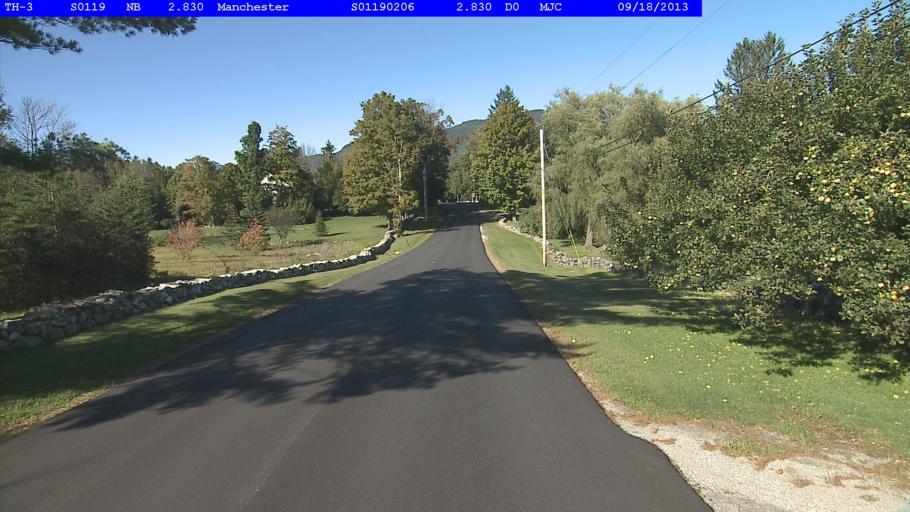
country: US
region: Vermont
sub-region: Bennington County
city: Manchester Center
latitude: 43.2038
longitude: -73.0689
